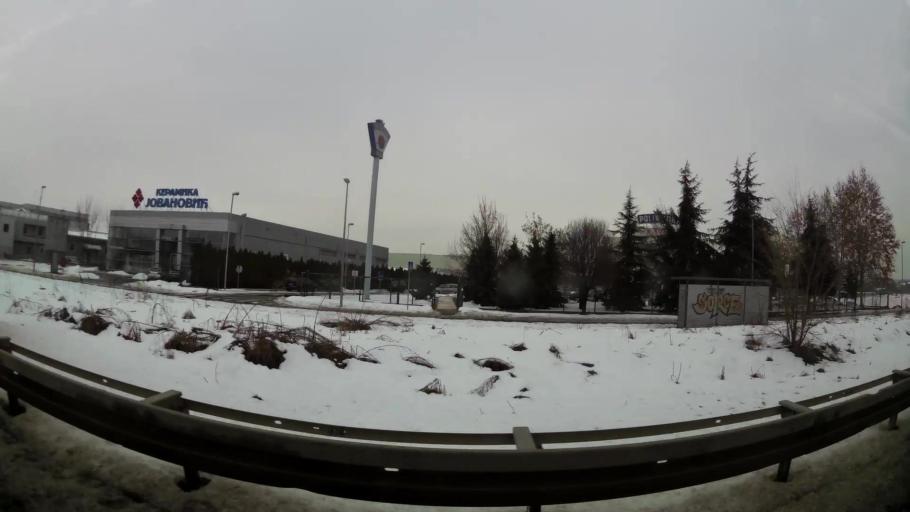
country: RS
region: Central Serbia
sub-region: Belgrade
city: Zemun
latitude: 44.8632
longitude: 20.3500
